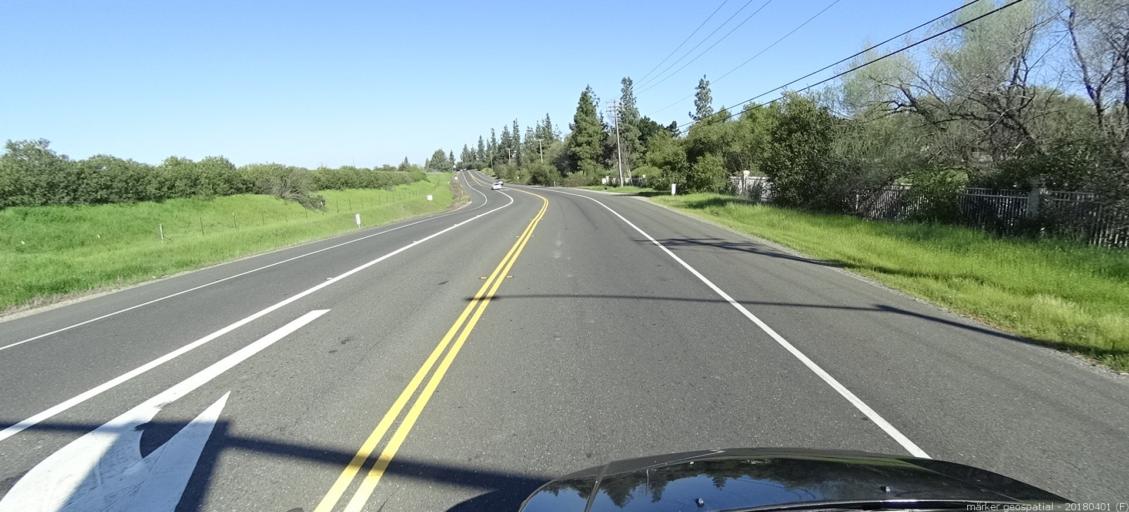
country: US
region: California
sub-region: Sacramento County
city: Rancho Murieta
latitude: 38.4876
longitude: -121.0829
